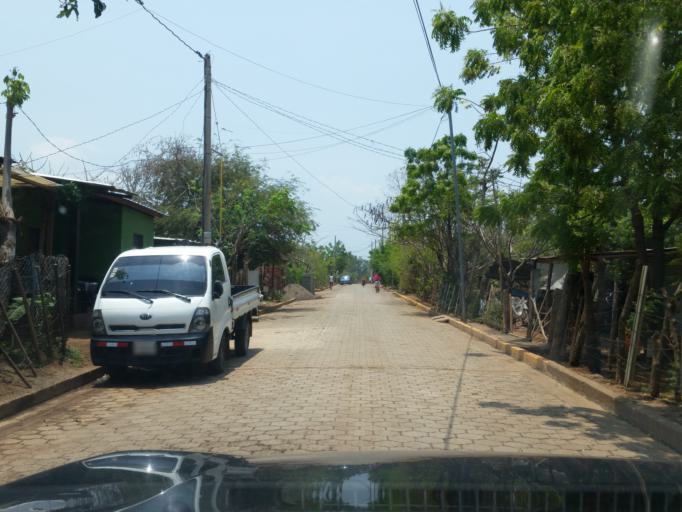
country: NI
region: Granada
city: Granada
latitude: 11.9098
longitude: -85.9601
